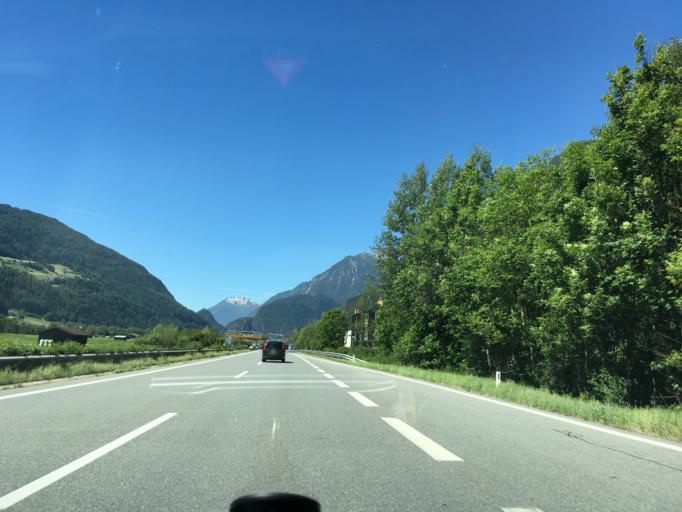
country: AT
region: Tyrol
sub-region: Politischer Bezirk Imst
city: Imsterberg
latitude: 47.2130
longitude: 10.6928
